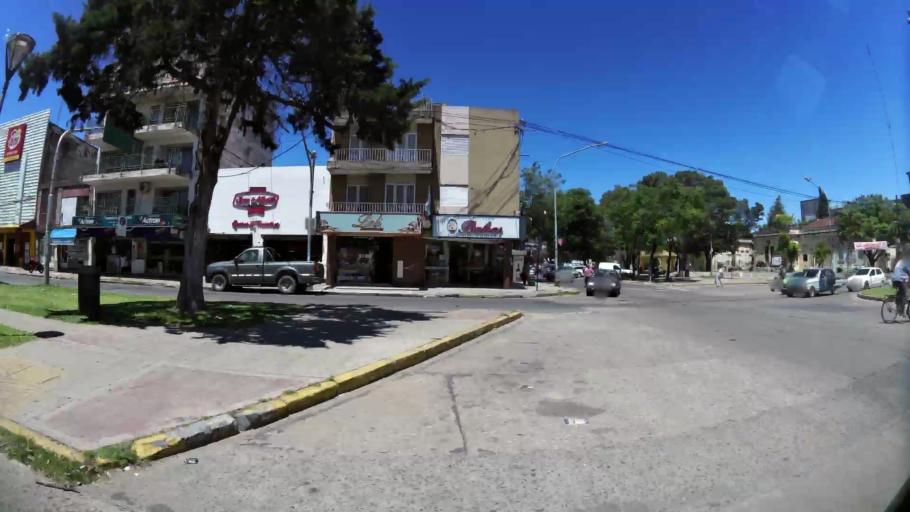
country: AR
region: Santa Fe
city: Santa Fe de la Vera Cruz
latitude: -31.6331
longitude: -60.7147
